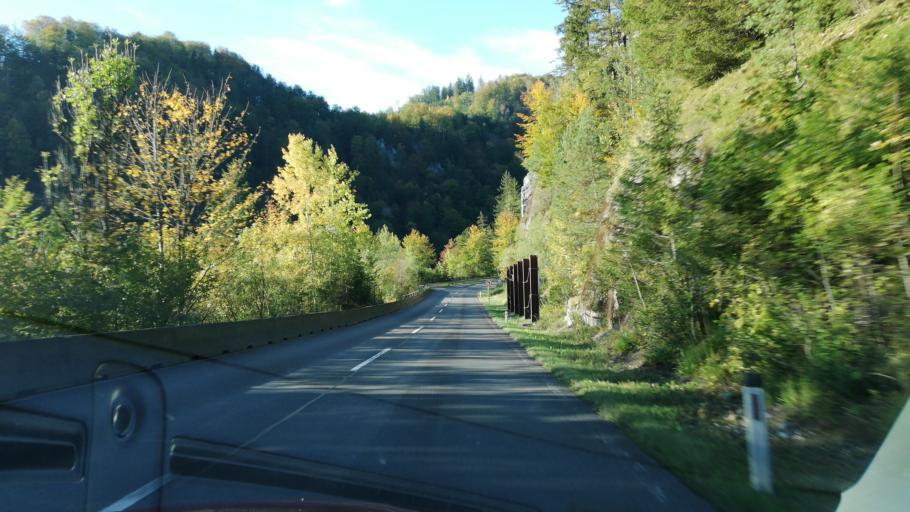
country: AT
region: Styria
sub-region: Politischer Bezirk Liezen
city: Altenmarkt bei Sankt Gallen
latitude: 47.7277
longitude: 14.6494
